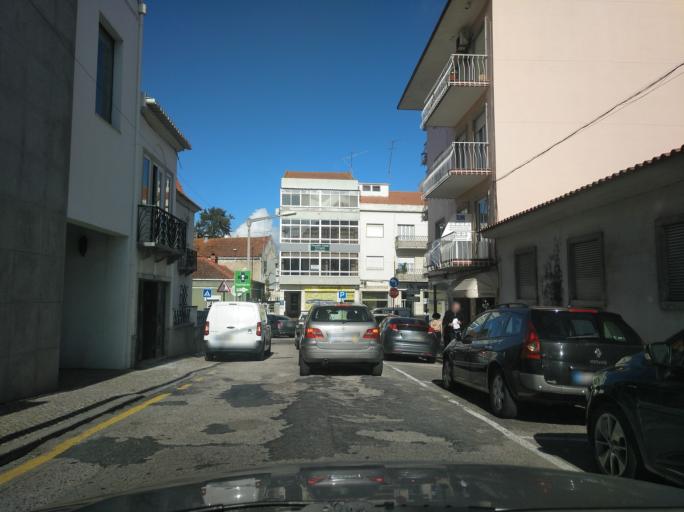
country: PT
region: Lisbon
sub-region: Loures
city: Loures
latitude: 38.8295
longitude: -9.1667
